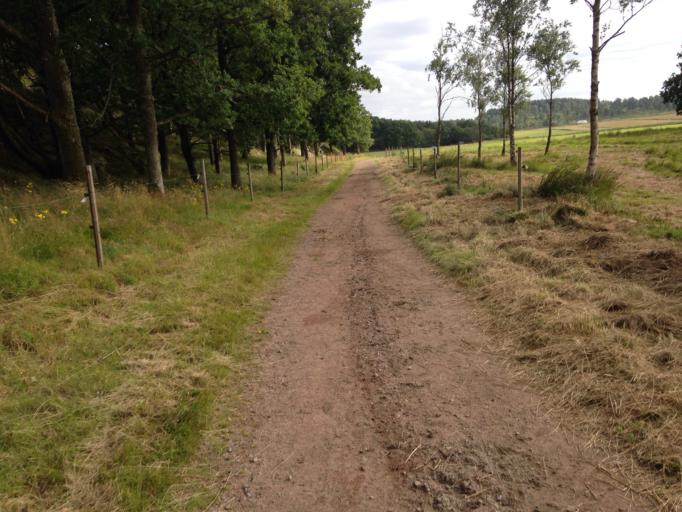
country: SE
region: Vaestra Goetaland
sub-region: Kungalvs Kommun
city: Kungalv
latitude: 57.8132
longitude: 11.8860
